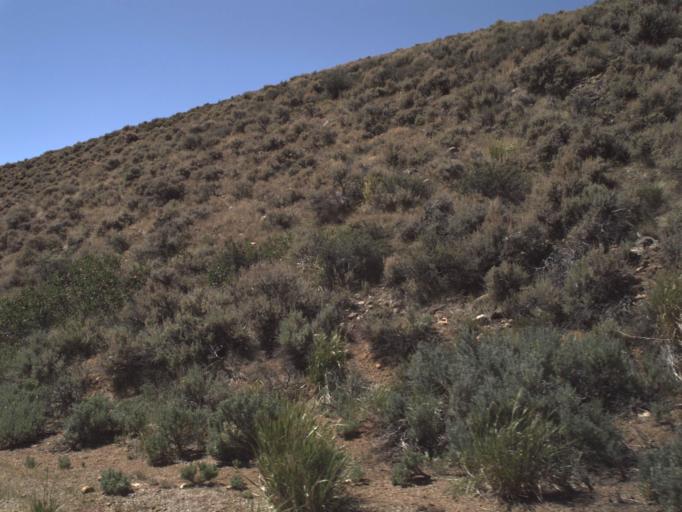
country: US
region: Utah
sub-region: Rich County
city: Randolph
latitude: 41.4790
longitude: -111.3538
